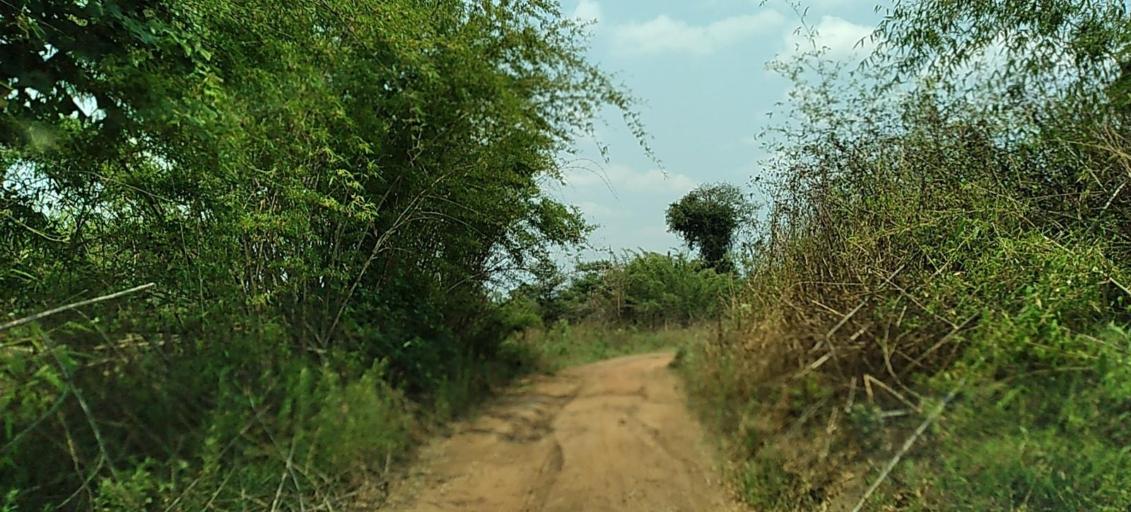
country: ZM
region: Copperbelt
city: Kalulushi
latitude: -12.7586
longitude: 28.0238
